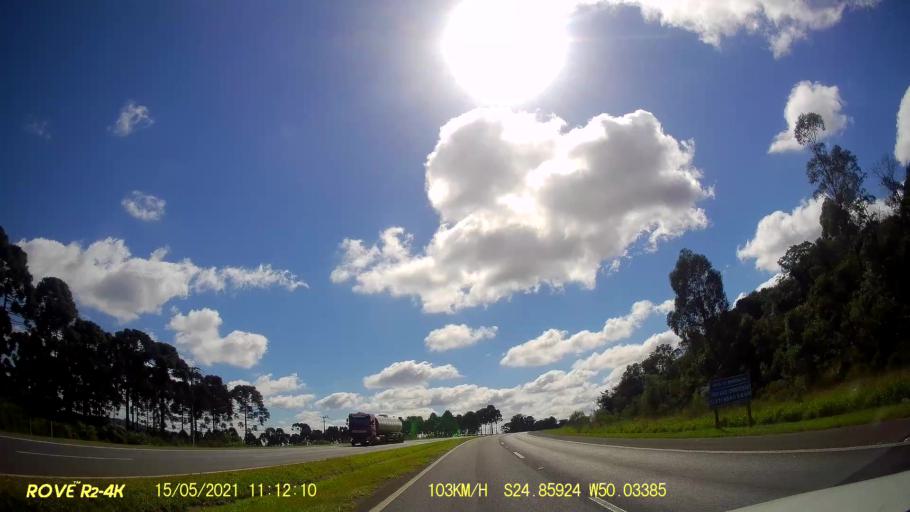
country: BR
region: Parana
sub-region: Castro
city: Castro
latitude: -24.8586
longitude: -50.0342
